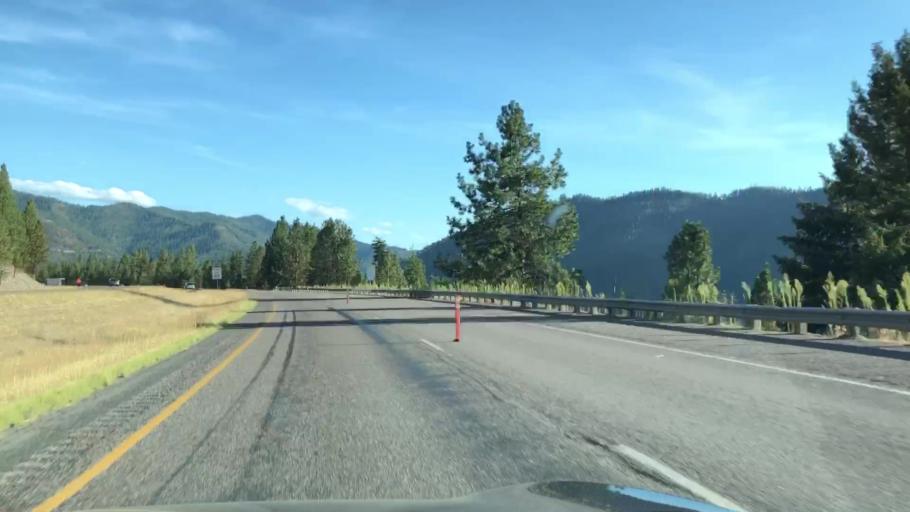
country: US
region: Montana
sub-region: Mineral County
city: Superior
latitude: 47.0204
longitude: -114.7352
